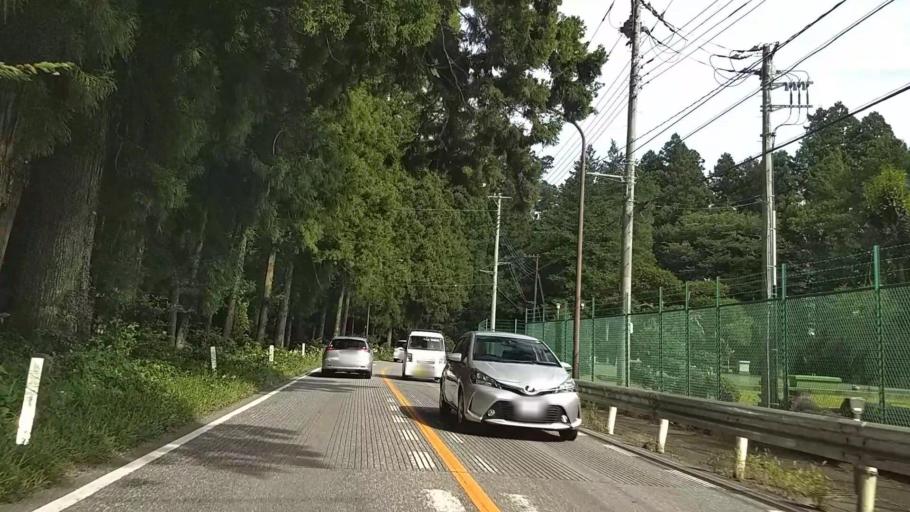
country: JP
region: Tochigi
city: Imaichi
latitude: 36.7275
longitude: 139.6798
